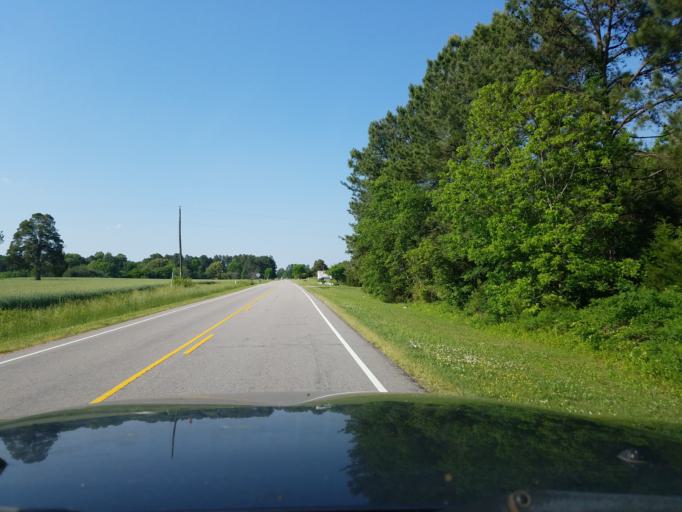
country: US
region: North Carolina
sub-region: Vance County
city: Henderson
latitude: 36.3712
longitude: -78.3722
